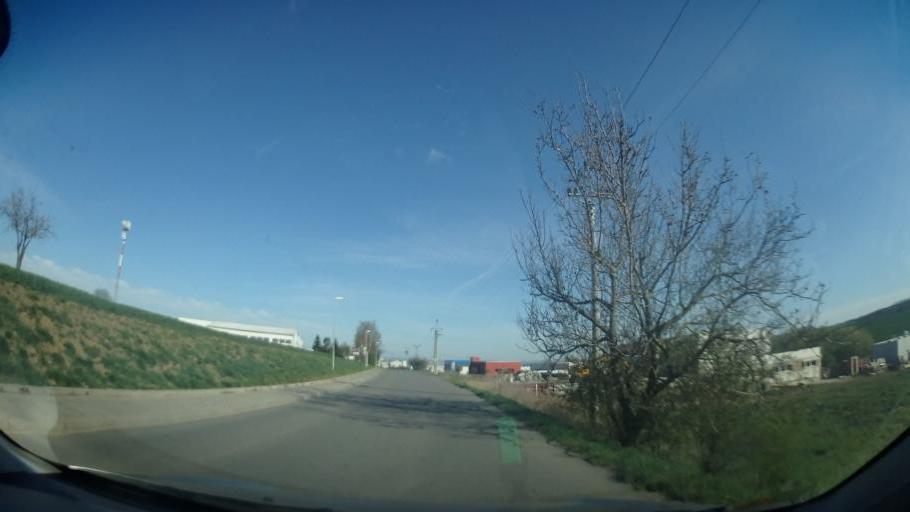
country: CZ
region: South Moravian
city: Moravany
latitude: 49.1461
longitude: 16.5847
